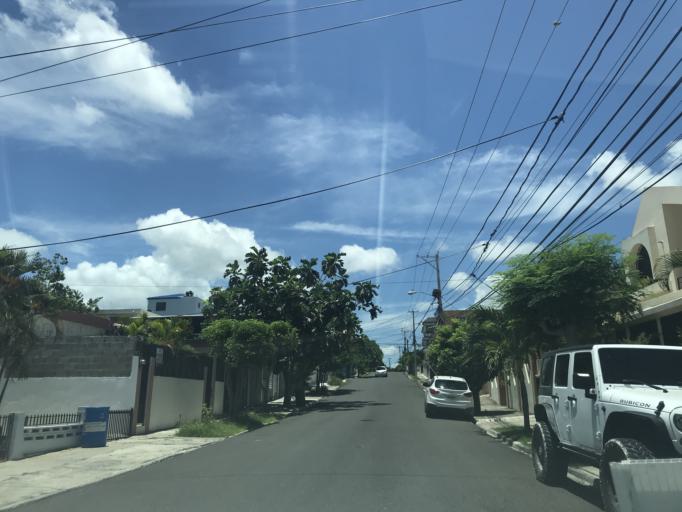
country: DO
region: Santiago
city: Santiago de los Caballeros
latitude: 19.4414
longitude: -70.6974
